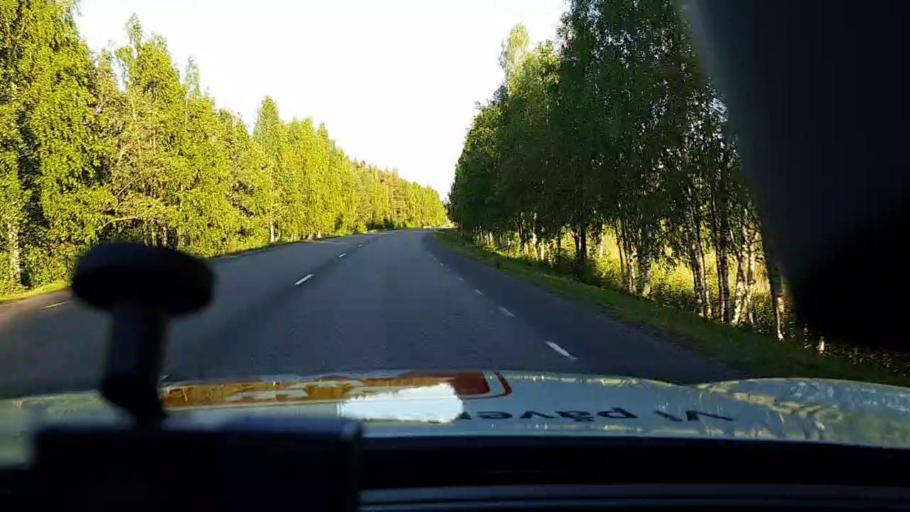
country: SE
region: Norrbotten
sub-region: Lulea Kommun
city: Lulea
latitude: 65.6116
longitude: 22.1625
